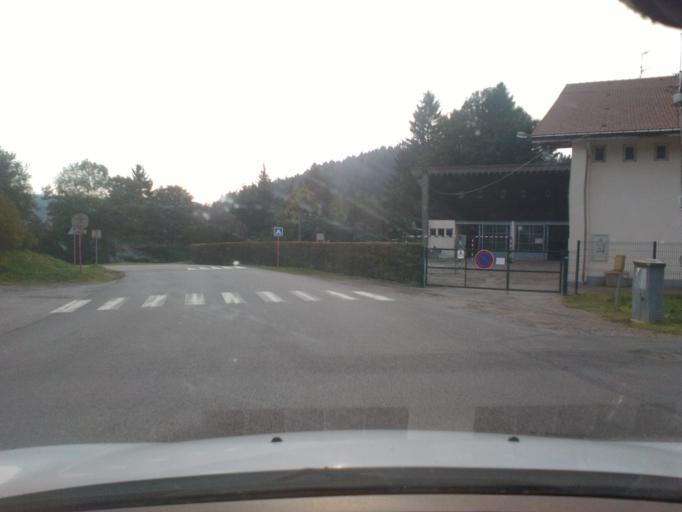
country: FR
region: Lorraine
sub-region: Departement des Vosges
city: Gerardmer
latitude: 48.0502
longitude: 6.8706
